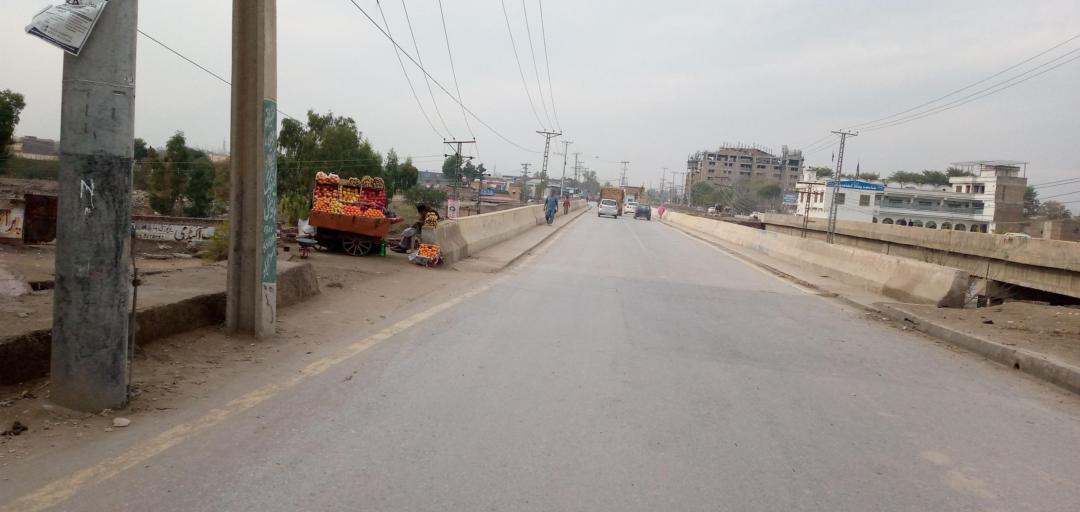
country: PK
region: Khyber Pakhtunkhwa
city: Peshawar
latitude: 34.0032
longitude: 71.4671
